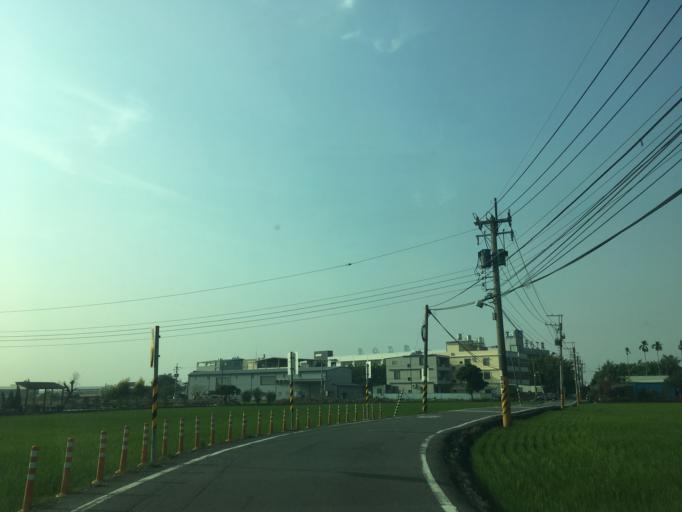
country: TW
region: Taiwan
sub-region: Taichung City
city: Taichung
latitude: 24.0559
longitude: 120.6807
